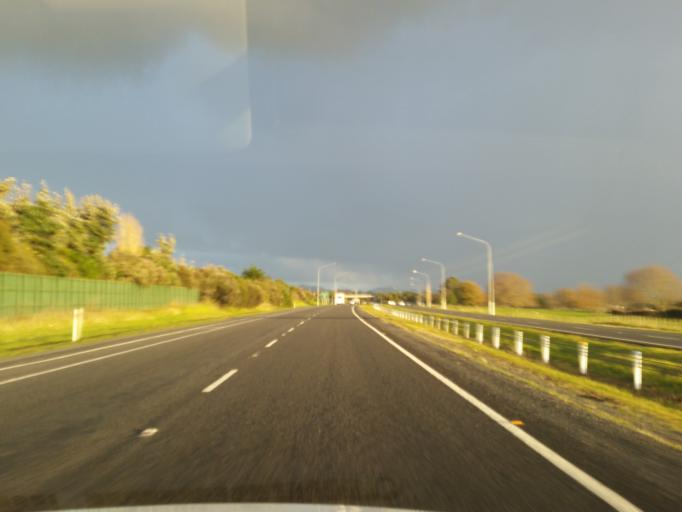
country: NZ
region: Waikato
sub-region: Waikato District
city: Te Kauwhata
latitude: -37.4831
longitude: 175.1604
